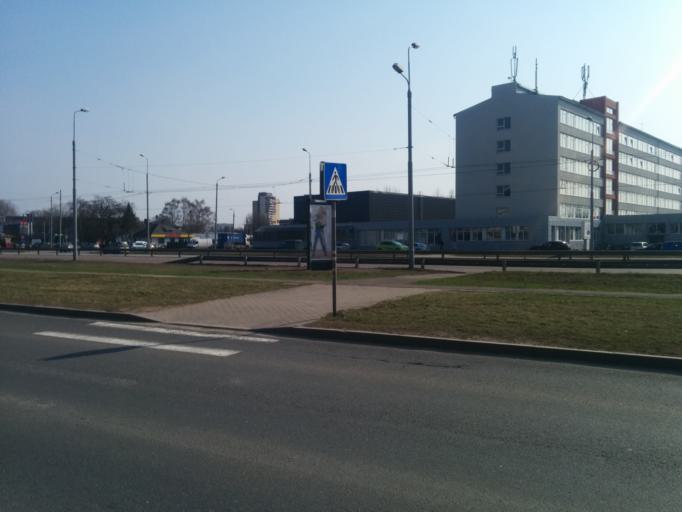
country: LV
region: Riga
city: Riga
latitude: 56.9655
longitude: 24.1633
